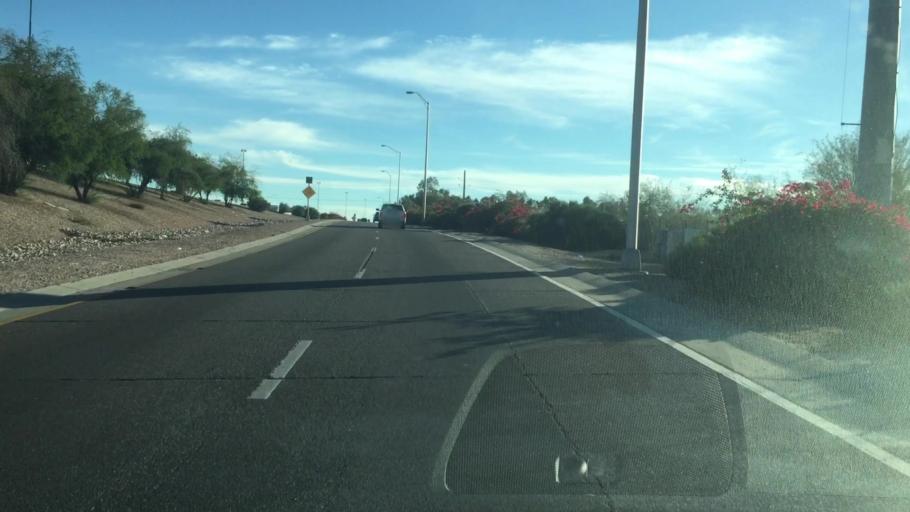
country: US
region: Arizona
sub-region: Maricopa County
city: Guadalupe
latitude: 33.3774
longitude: -111.9686
